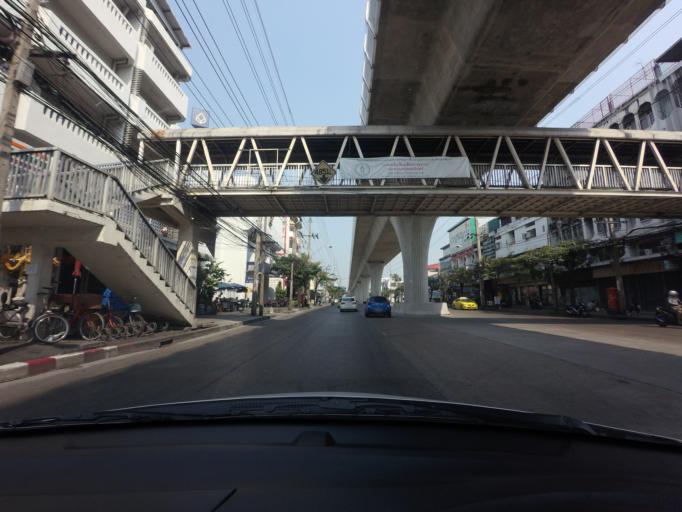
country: TH
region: Bangkok
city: Bangkok Noi
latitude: 13.7485
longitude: 100.4699
